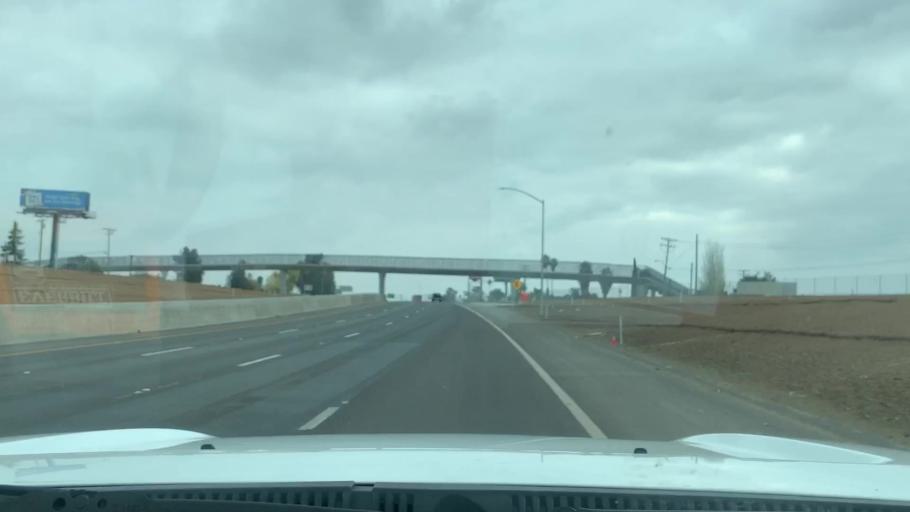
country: US
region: California
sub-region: Tulare County
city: Goshen
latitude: 36.3501
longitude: -119.4268
